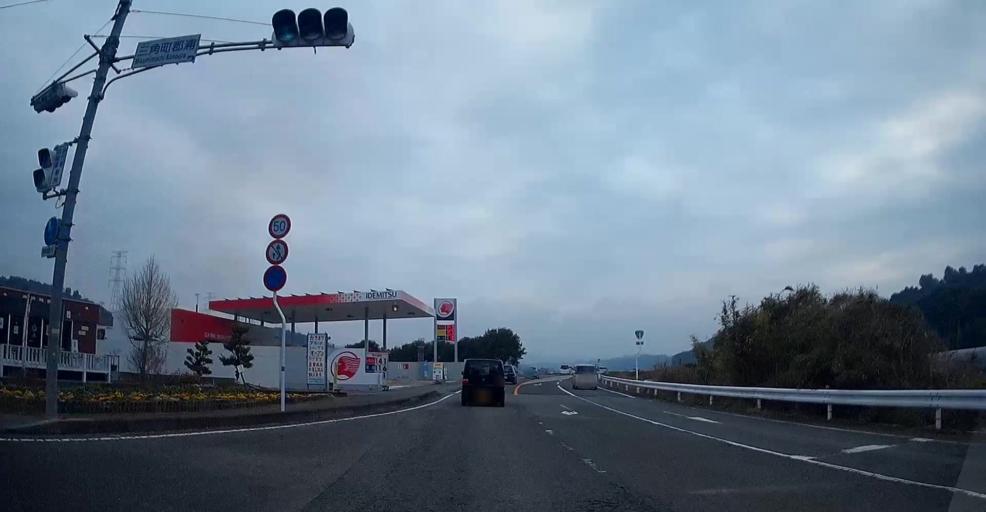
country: JP
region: Kumamoto
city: Yatsushiro
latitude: 32.6243
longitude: 130.5173
